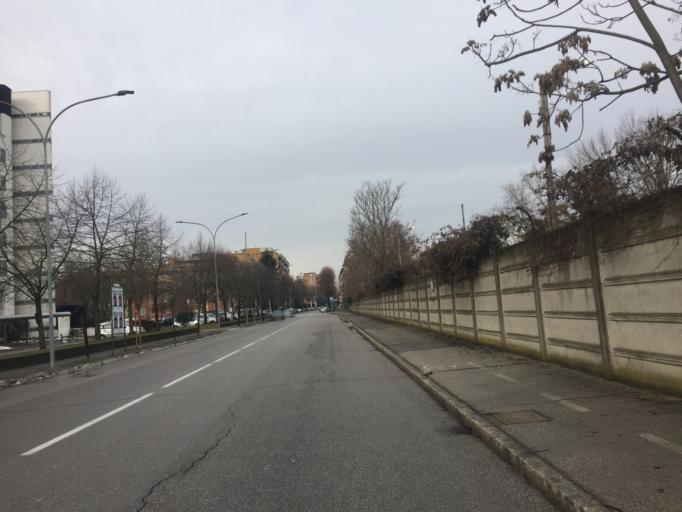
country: IT
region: Emilia-Romagna
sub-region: Provincia di Bologna
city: Bologna
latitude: 44.5092
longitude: 11.3061
